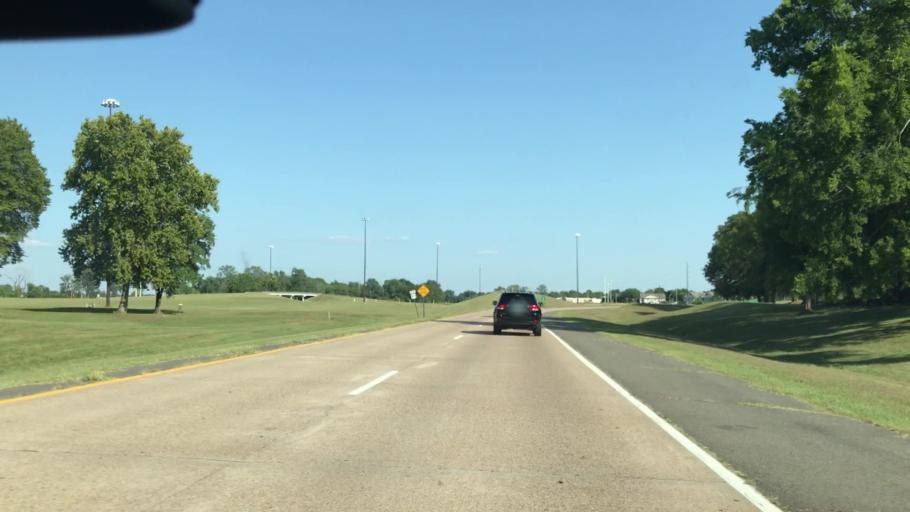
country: US
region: Louisiana
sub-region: Bossier Parish
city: Bossier City
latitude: 32.5056
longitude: -93.7194
